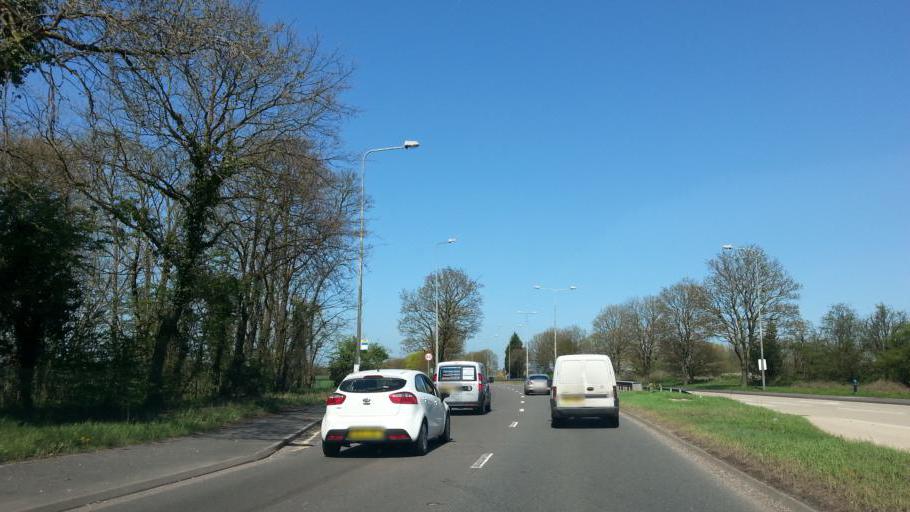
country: GB
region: England
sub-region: Staffordshire
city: Brewood
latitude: 52.6726
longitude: -2.1306
